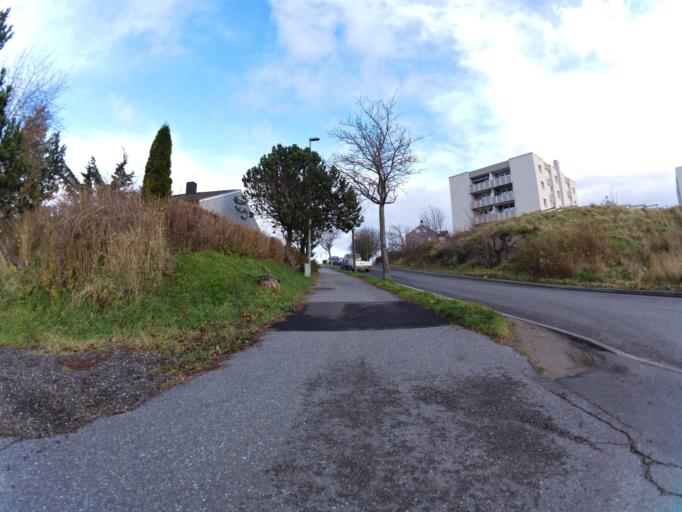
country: NO
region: Ostfold
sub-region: Sarpsborg
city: Sarpsborg
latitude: 59.2719
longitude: 11.0838
